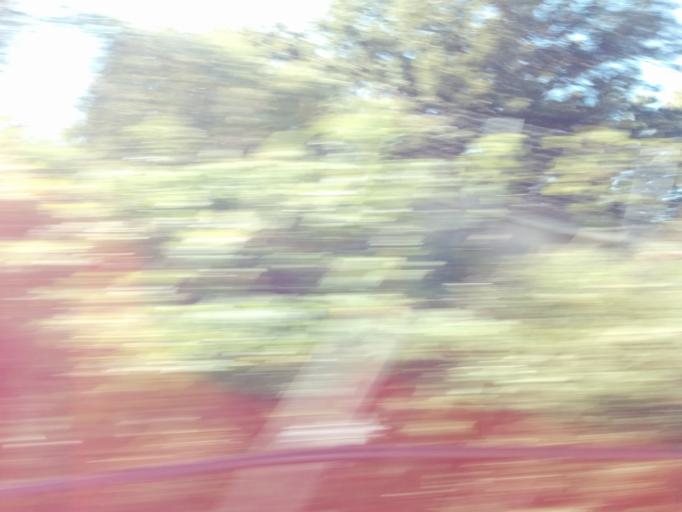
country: JP
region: Aichi
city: Obu
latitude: 35.0488
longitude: 136.9532
